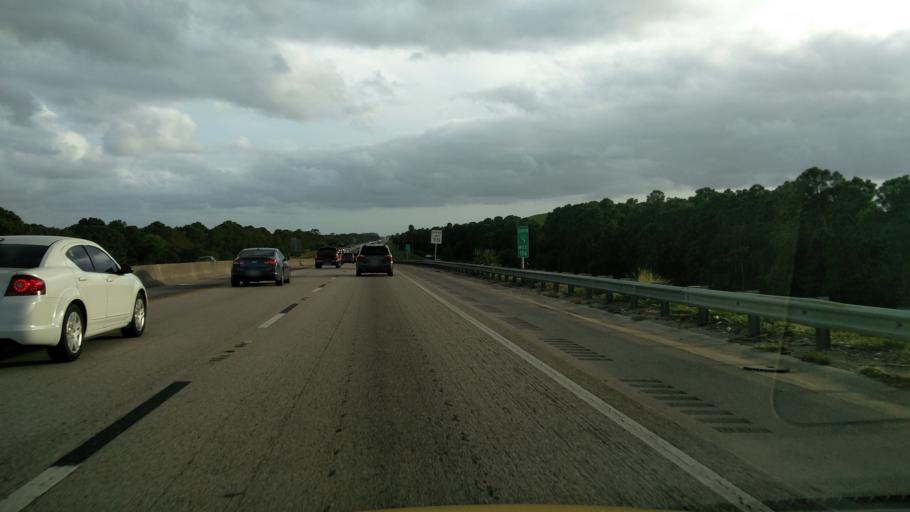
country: US
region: Florida
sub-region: Palm Beach County
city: Palm Beach Gardens
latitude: 26.7937
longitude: -80.1318
